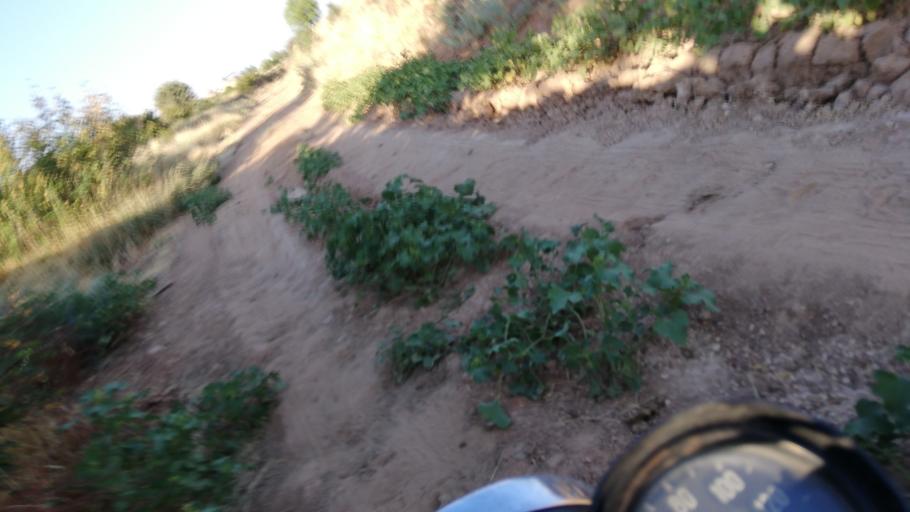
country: TR
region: Mardin
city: Kindirip
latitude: 37.4453
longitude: 41.2111
